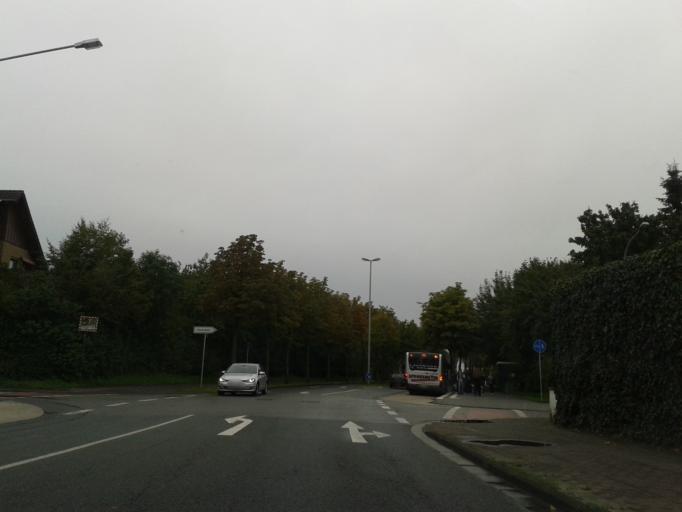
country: DE
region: North Rhine-Westphalia
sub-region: Regierungsbezirk Detmold
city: Paderborn
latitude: 51.7390
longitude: 8.7666
